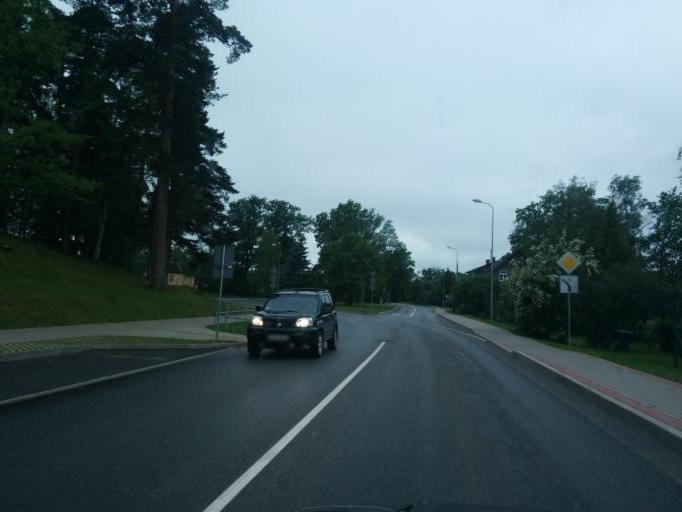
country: LV
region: Smiltene
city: Smiltene
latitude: 57.4255
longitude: 25.8959
